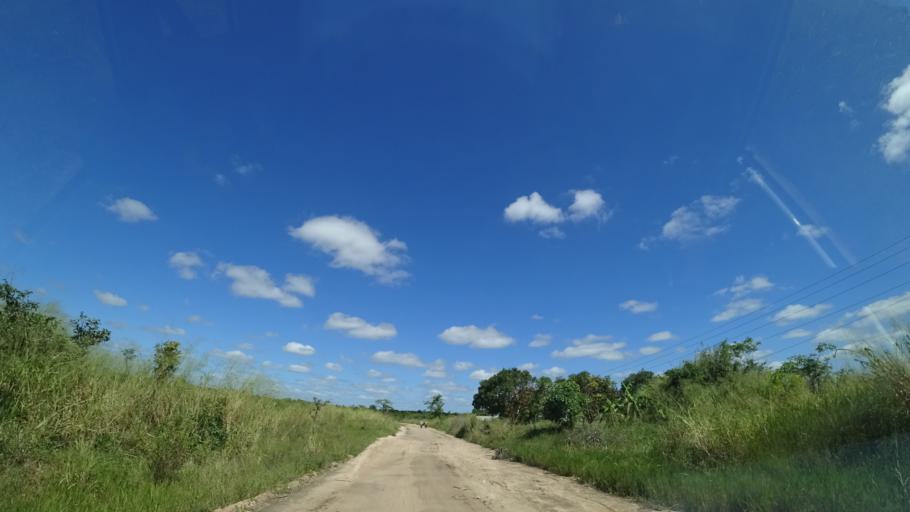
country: MZ
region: Sofala
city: Dondo
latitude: -19.3142
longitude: 34.6913
